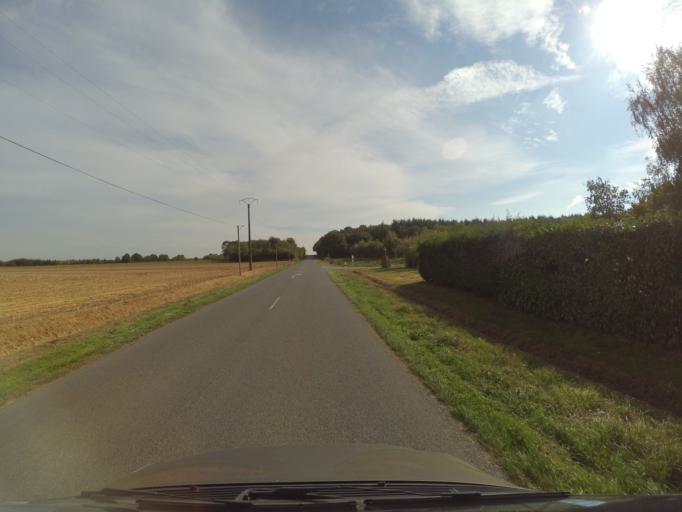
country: FR
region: Pays de la Loire
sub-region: Departement de Maine-et-Loire
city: Geste
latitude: 47.1830
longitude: -1.0745
